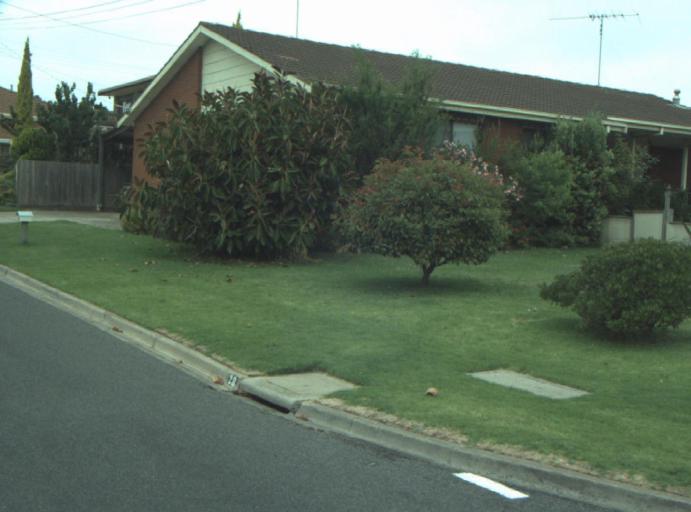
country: AU
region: Victoria
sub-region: Greater Geelong
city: Clifton Springs
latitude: -38.1489
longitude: 144.5744
